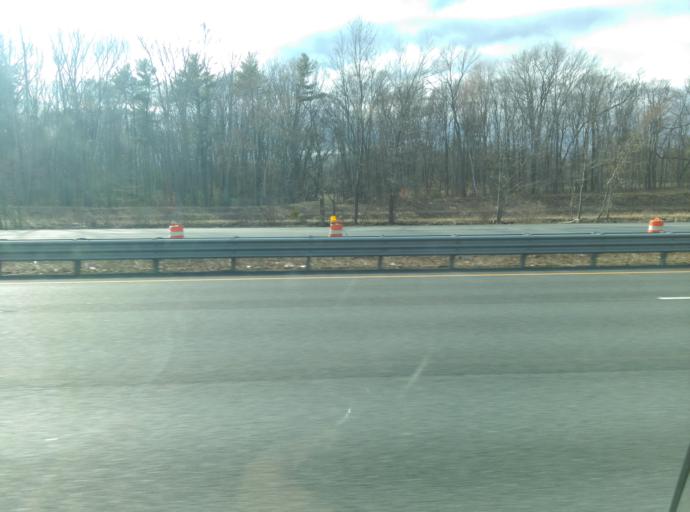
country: US
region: Massachusetts
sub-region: Essex County
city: Amesbury
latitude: 42.8544
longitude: -70.8974
